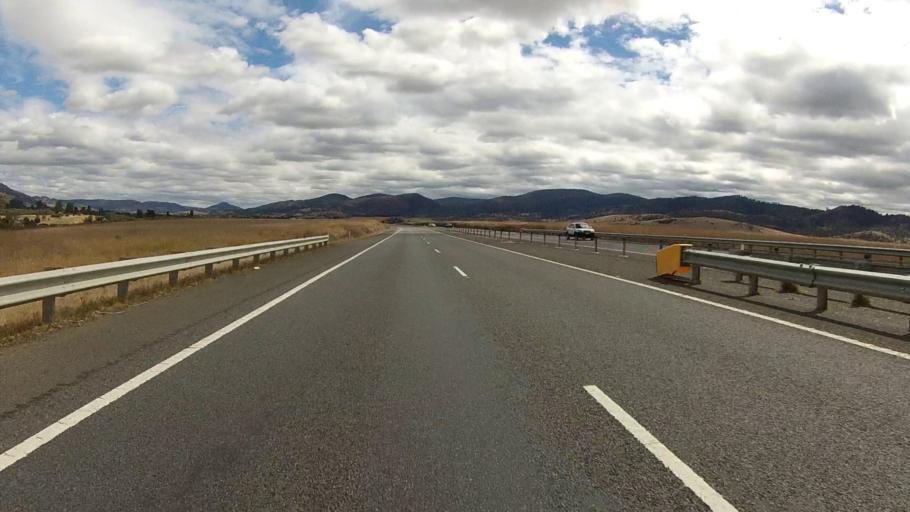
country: AU
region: Tasmania
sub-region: Brighton
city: Bridgewater
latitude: -42.6879
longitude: 147.2783
